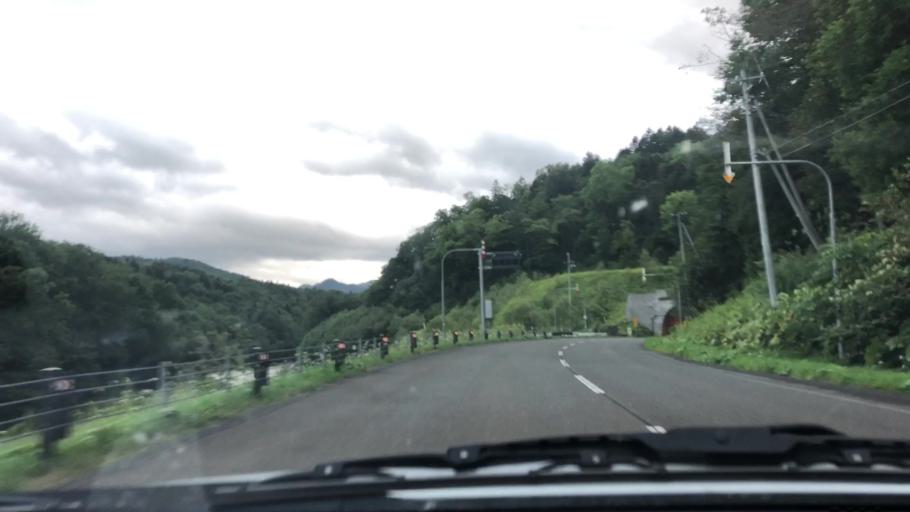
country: JP
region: Hokkaido
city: Shimo-furano
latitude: 42.9632
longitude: 142.3753
